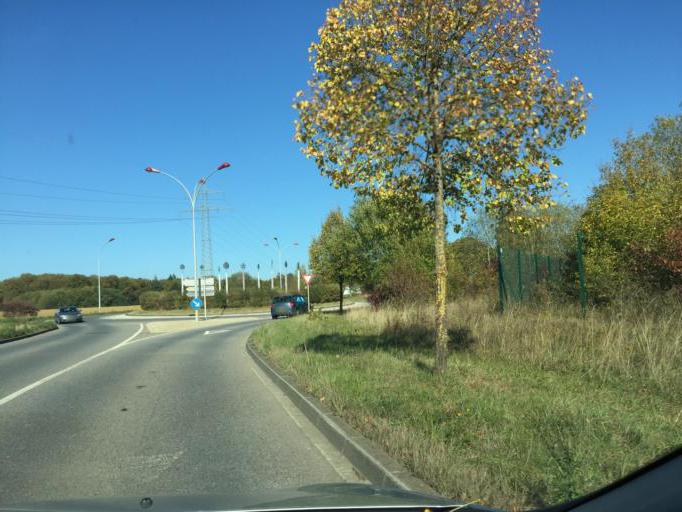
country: LU
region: Luxembourg
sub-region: Canton de Luxembourg
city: Strassen
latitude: 49.6323
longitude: 6.0646
